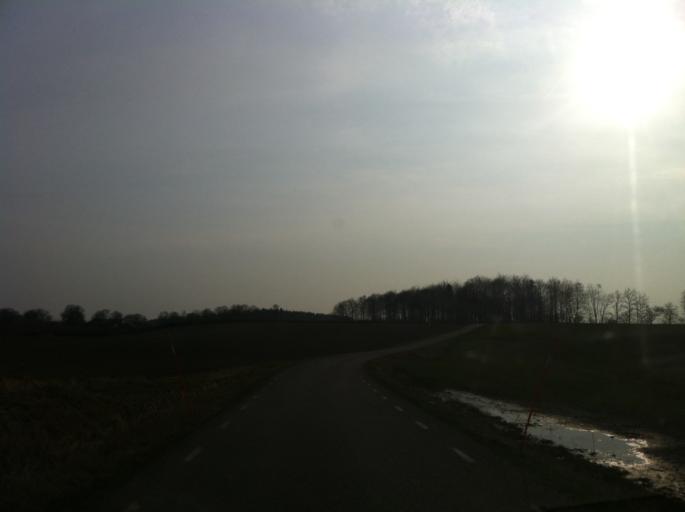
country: SE
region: Skane
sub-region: Eslovs Kommun
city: Stehag
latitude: 55.9596
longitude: 13.3165
